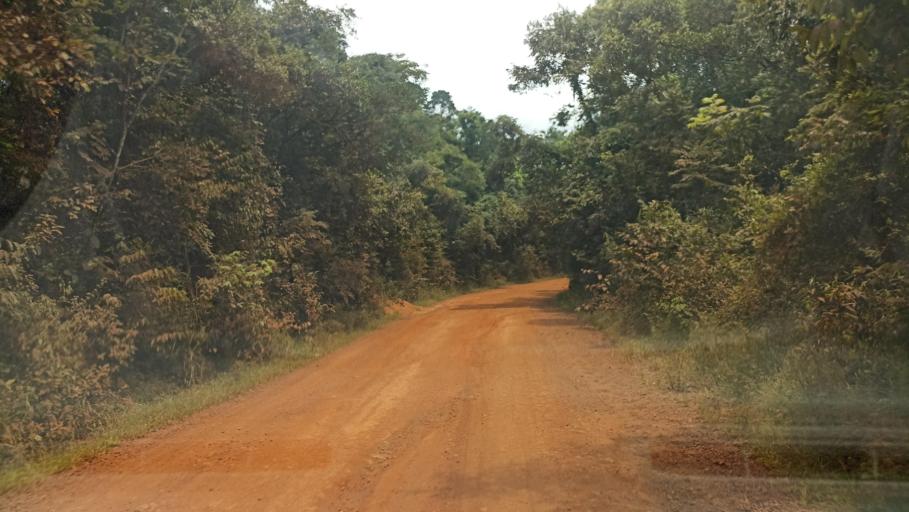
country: BR
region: Minas Gerais
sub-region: Itabirito
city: Itabirito
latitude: -20.3403
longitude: -43.7540
